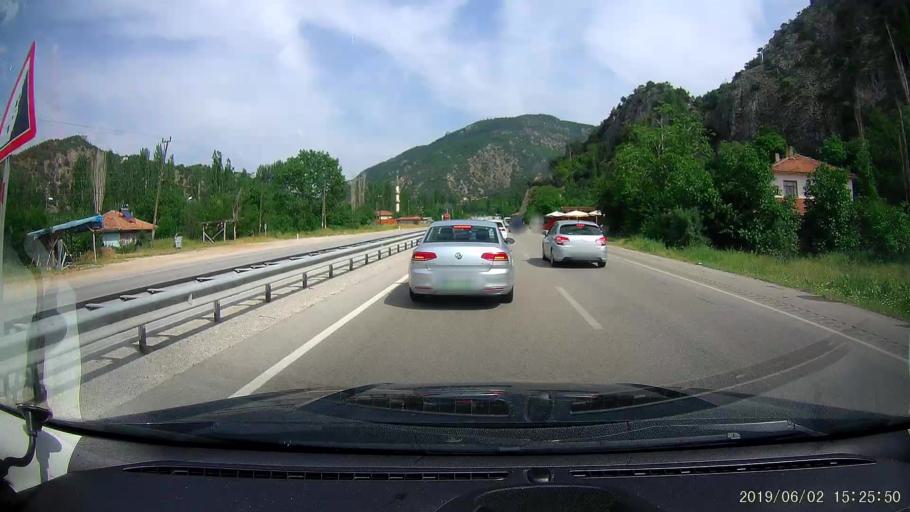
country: TR
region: Amasya
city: Saraycik
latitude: 40.9904
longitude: 35.0270
